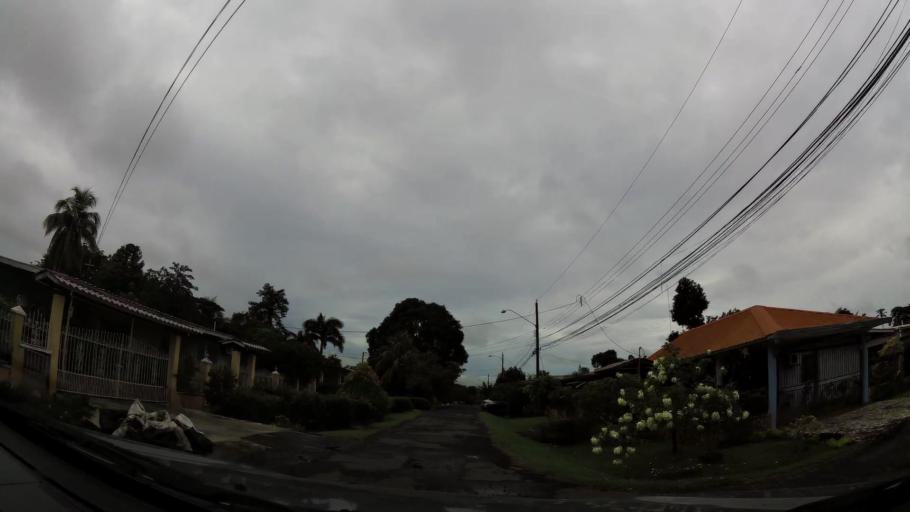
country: PA
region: Chiriqui
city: David
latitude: 8.4247
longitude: -82.4507
